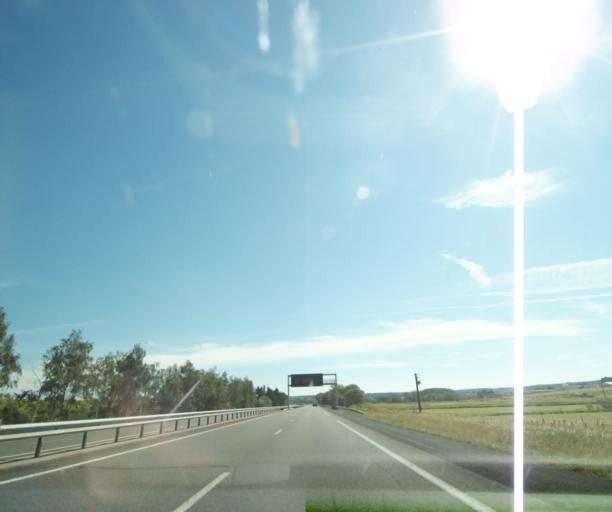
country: FR
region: Lorraine
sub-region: Departement des Vosges
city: Bulgneville
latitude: 48.2064
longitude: 5.8058
